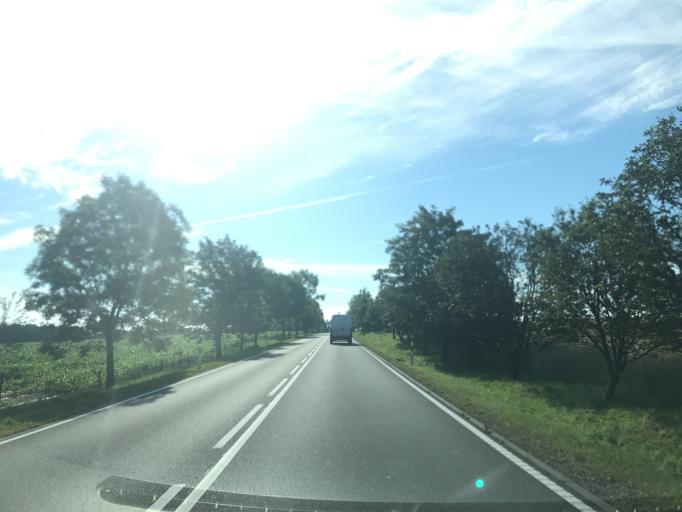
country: PL
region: Pomeranian Voivodeship
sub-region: Powiat czluchowski
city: Rzeczenica
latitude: 53.7483
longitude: 17.1650
